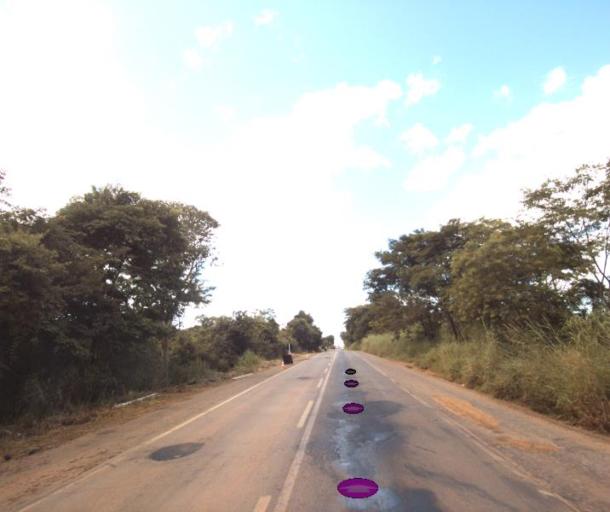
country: BR
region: Goias
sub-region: Petrolina De Goias
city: Petrolina de Goias
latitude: -16.0073
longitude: -49.1293
